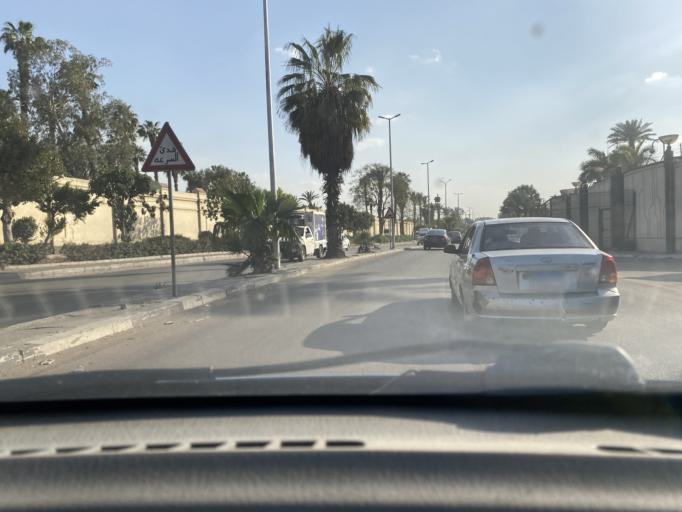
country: EG
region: Muhafazat al Qahirah
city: Cairo
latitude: 30.0972
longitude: 31.2985
